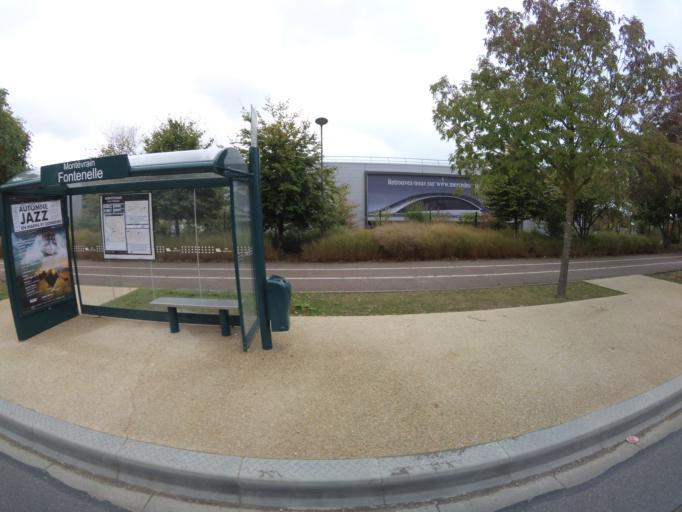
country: FR
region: Ile-de-France
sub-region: Departement de Seine-et-Marne
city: Chanteloup-en-Brie
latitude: 48.8540
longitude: 2.7594
